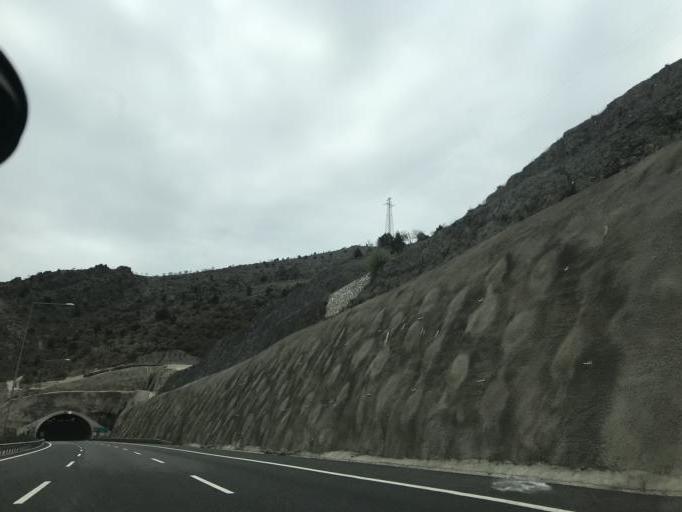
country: TR
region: Nigde
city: Ciftehan
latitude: 37.5481
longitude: 34.7831
